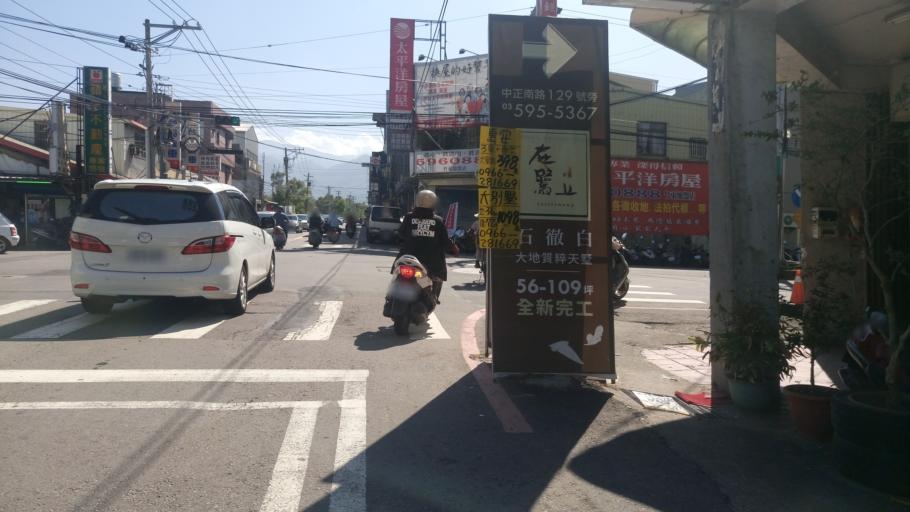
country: TW
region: Taiwan
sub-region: Hsinchu
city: Zhubei
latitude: 24.7297
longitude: 121.0915
